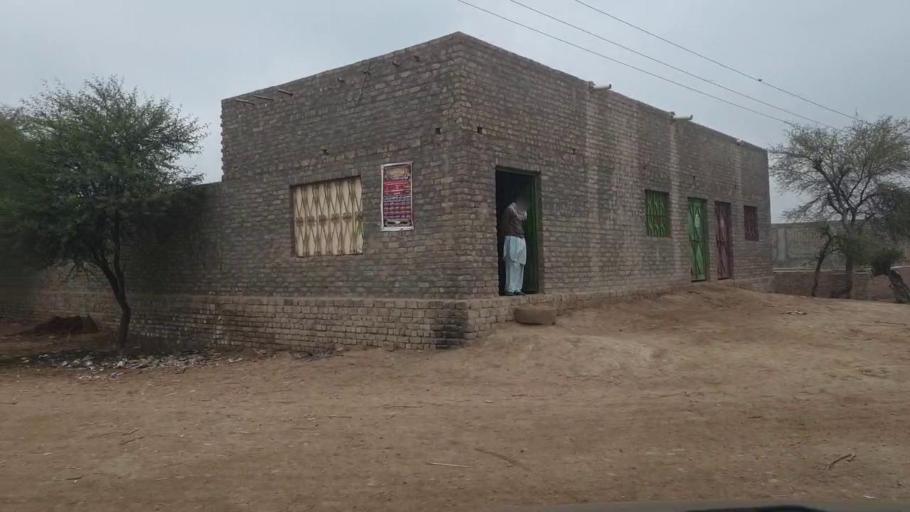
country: PK
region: Sindh
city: Shahdadpur
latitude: 25.9005
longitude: 68.6959
